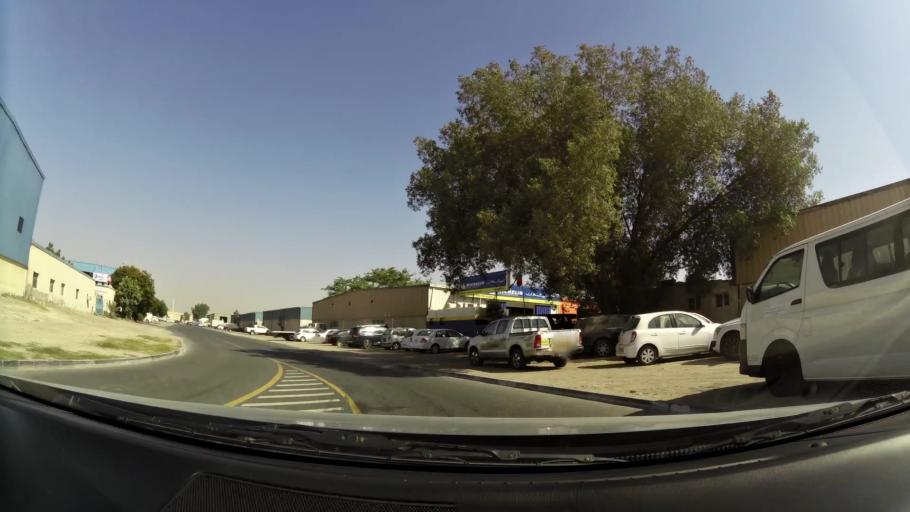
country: AE
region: Dubai
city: Dubai
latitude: 25.1165
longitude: 55.2140
